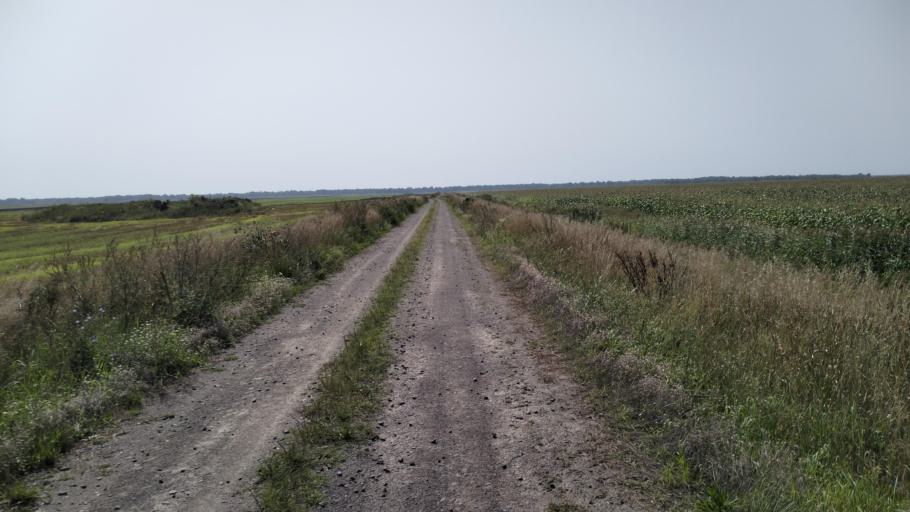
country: BY
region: Brest
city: Davyd-Haradok
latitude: 51.9897
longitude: 27.1643
